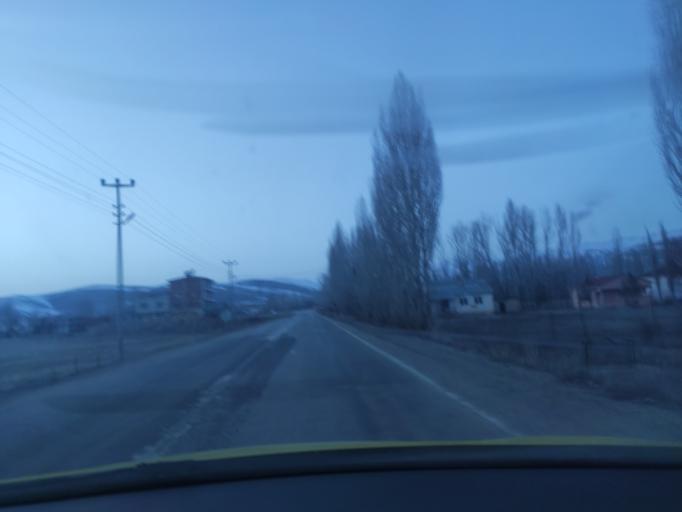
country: TR
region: Bayburt
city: Aydintepe
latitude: 40.3491
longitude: 40.1085
